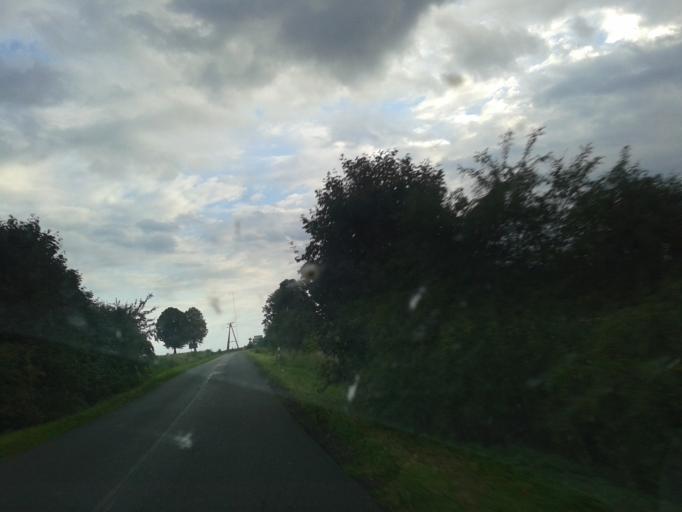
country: PL
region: West Pomeranian Voivodeship
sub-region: Powiat koszalinski
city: Bobolice
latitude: 53.8904
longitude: 16.5175
